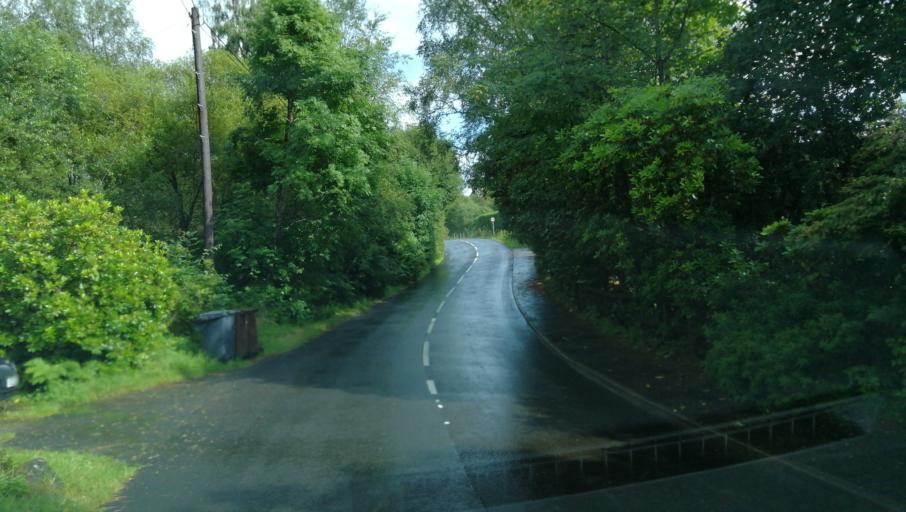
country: GB
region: Scotland
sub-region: Stirling
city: Callander
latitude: 56.2296
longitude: -4.3608
